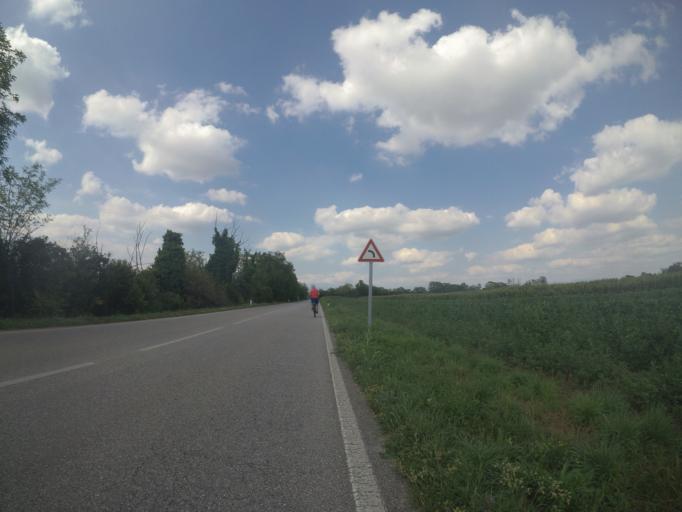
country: IT
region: Friuli Venezia Giulia
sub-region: Provincia di Udine
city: San Vito di Fagagna
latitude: 46.0761
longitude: 13.0853
